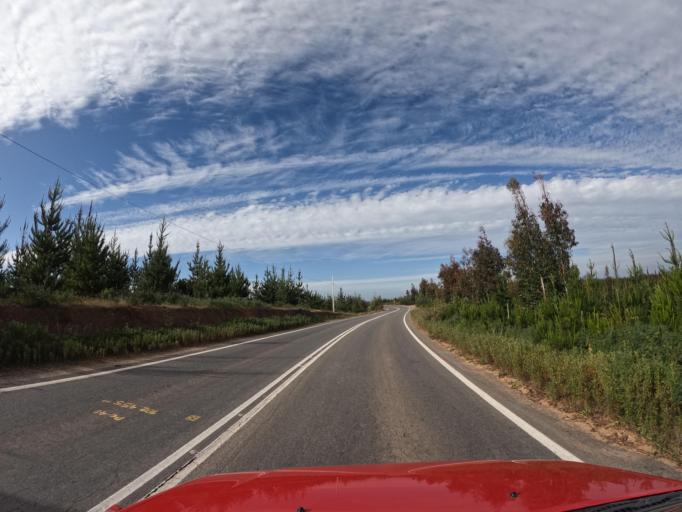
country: CL
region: O'Higgins
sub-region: Provincia de Colchagua
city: Santa Cruz
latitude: -34.3056
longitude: -71.8348
